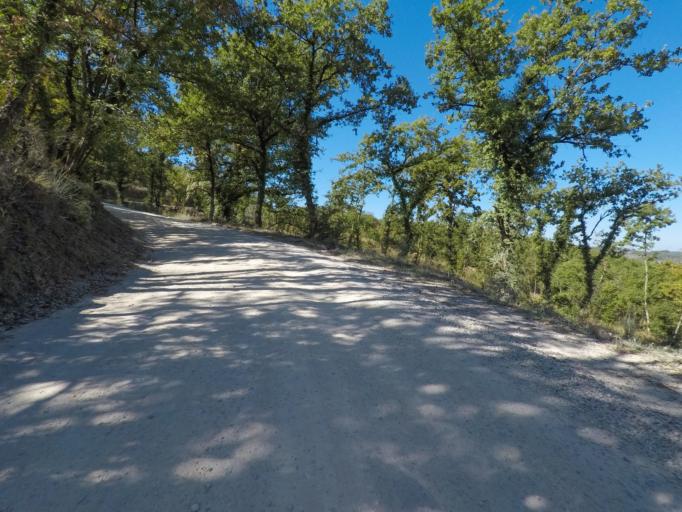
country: IT
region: Tuscany
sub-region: Provincia di Siena
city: Castellina in Chianti
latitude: 43.4358
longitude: 11.3204
